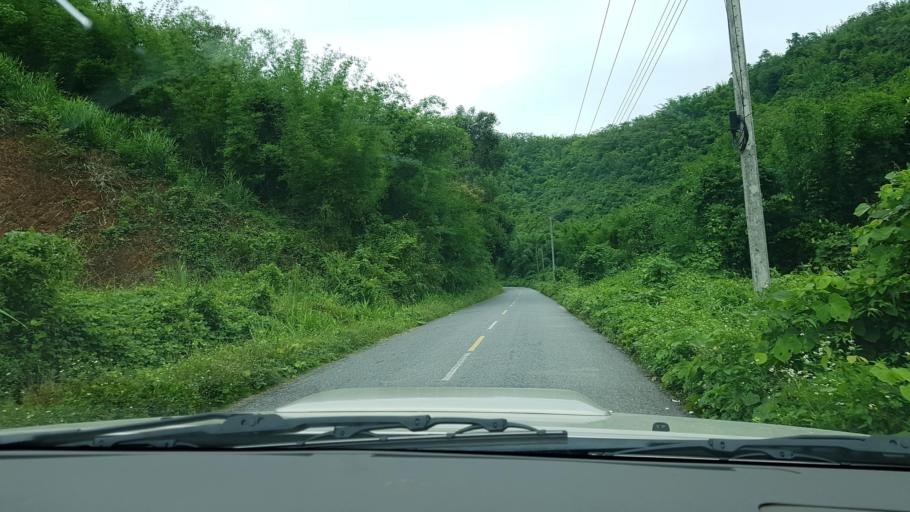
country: LA
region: Oudomxai
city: Muang La
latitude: 20.8980
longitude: 102.1812
